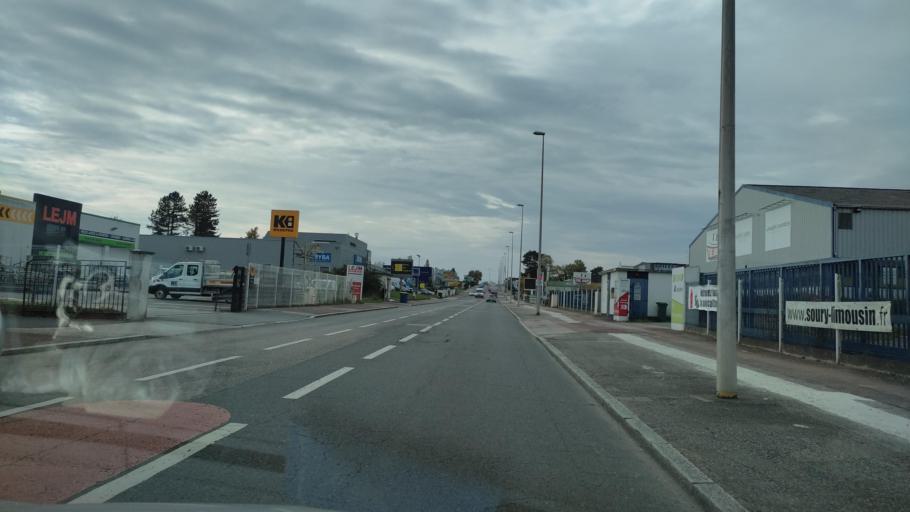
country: FR
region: Limousin
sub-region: Departement de la Haute-Vienne
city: Couzeix
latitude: 45.8760
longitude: 1.2723
